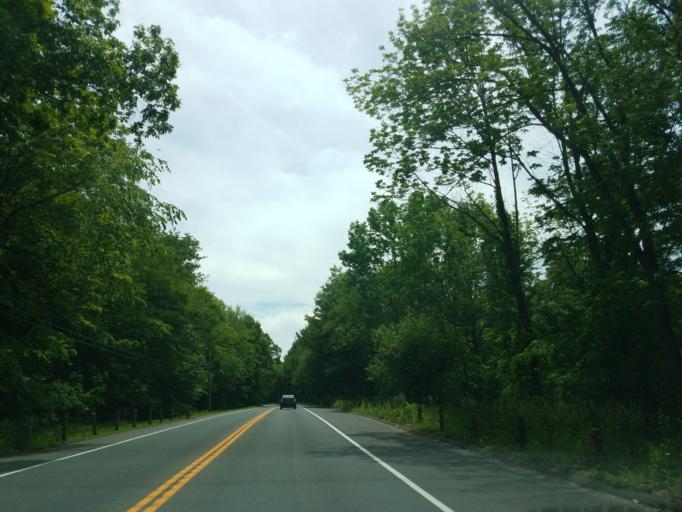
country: US
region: Connecticut
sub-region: Litchfield County
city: Northwest Harwinton
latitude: 41.7960
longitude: -73.0802
